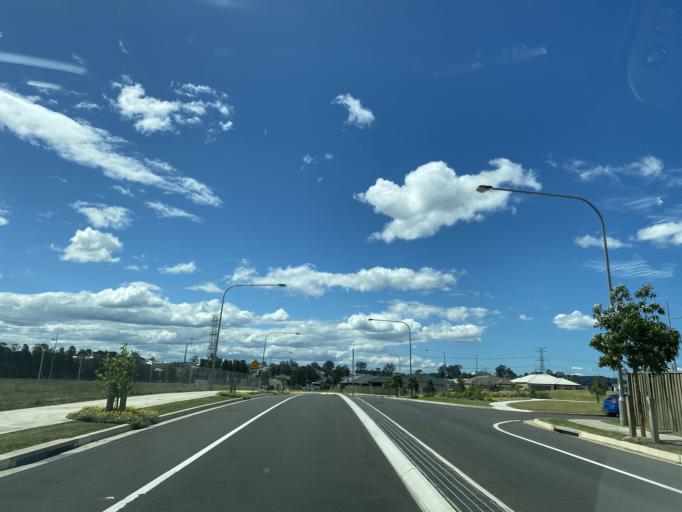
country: AU
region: New South Wales
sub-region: Camden
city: Narellan Vale
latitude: -34.0222
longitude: 150.7726
